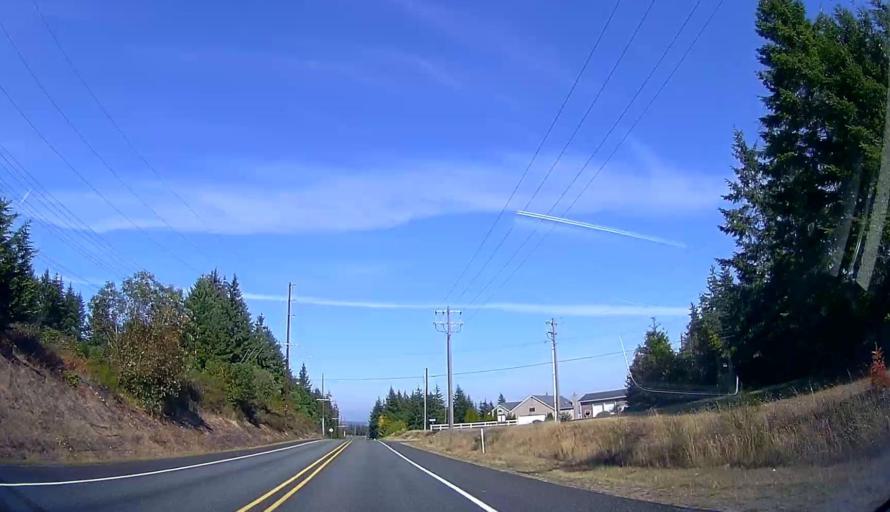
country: US
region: Washington
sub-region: Island County
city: Camano
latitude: 48.1919
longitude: -122.4905
